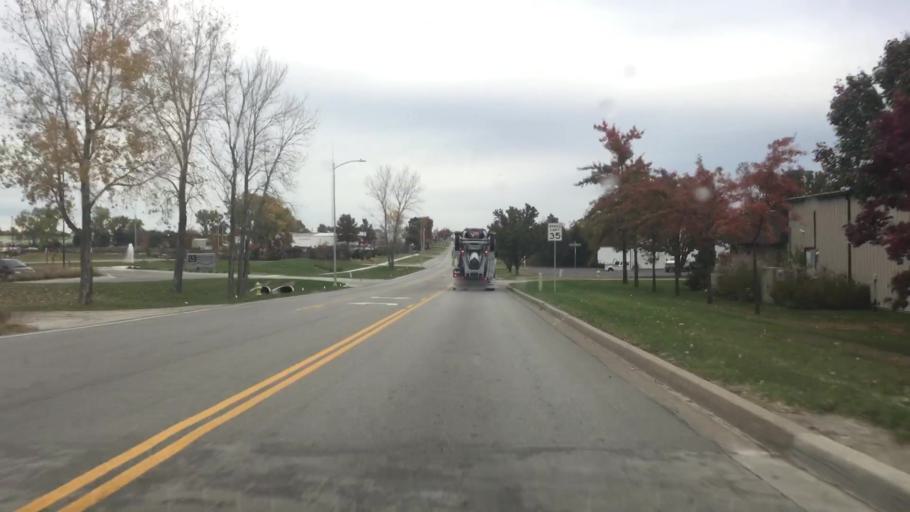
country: US
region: Missouri
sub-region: Jackson County
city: Lees Summit
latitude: 38.8962
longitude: -94.3634
